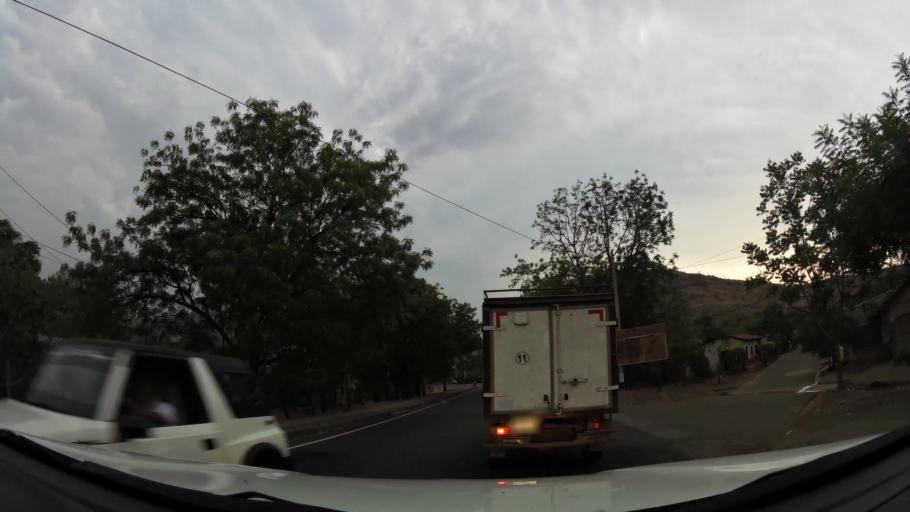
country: NI
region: Matagalpa
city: Ciudad Dario
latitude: 12.9294
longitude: -86.1971
